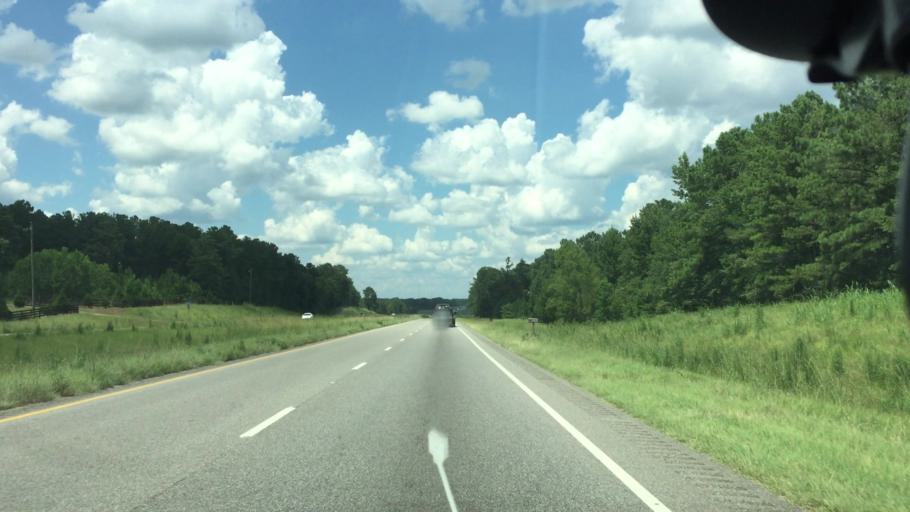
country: US
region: Alabama
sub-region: Montgomery County
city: Taylor
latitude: 32.0158
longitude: -86.0303
